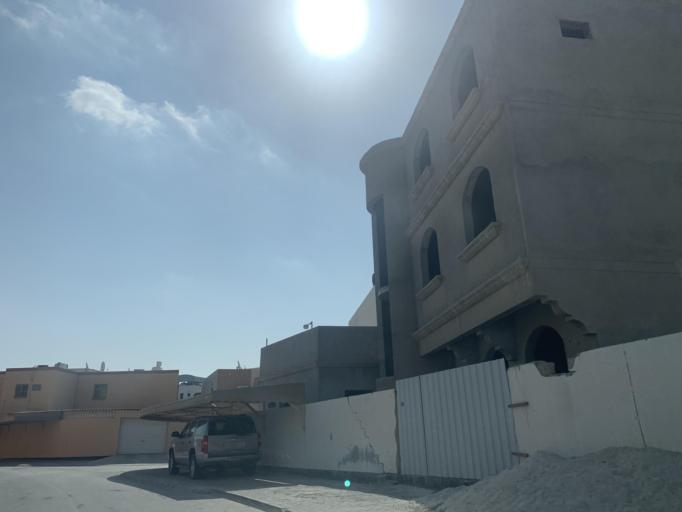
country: BH
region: Central Governorate
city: Madinat Hamad
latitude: 26.1257
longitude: 50.5021
